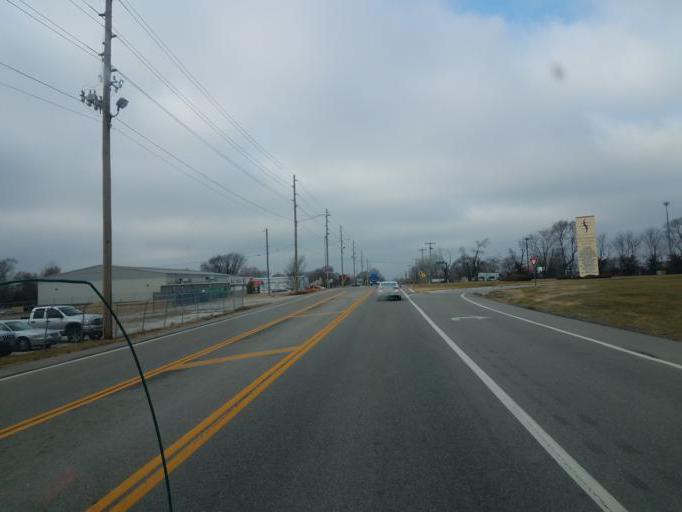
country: US
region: Missouri
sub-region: Greene County
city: Strafford
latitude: 37.2383
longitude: -93.2051
